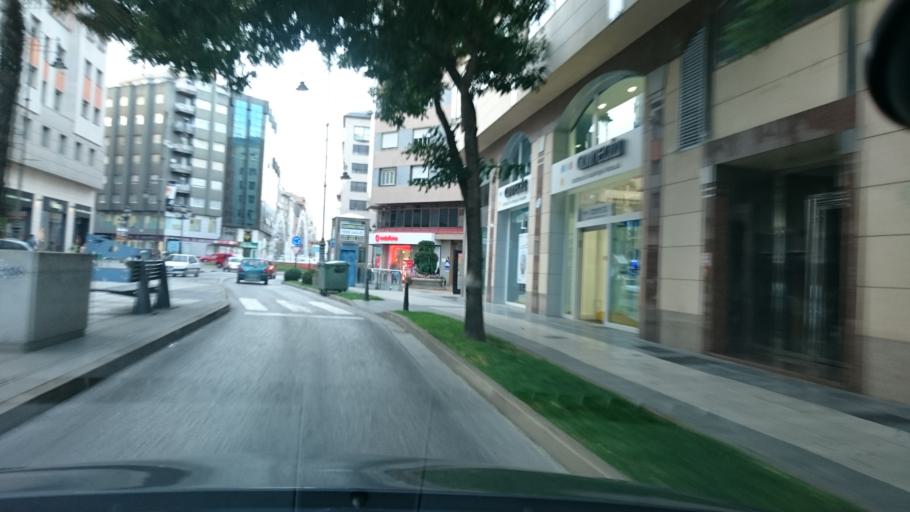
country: ES
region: Castille and Leon
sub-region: Provincia de Leon
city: Ponferrada
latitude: 42.5472
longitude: -6.5977
